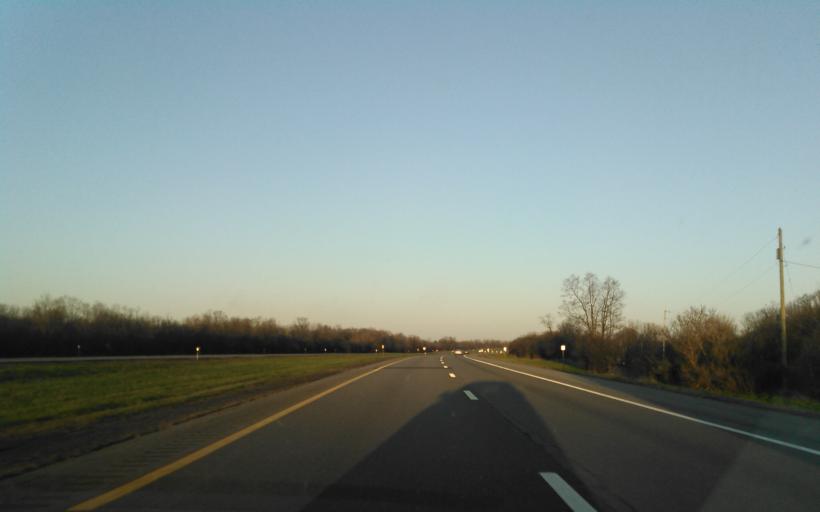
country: US
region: New York
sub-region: Ontario County
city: Phelps
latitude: 42.9738
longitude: -77.0913
